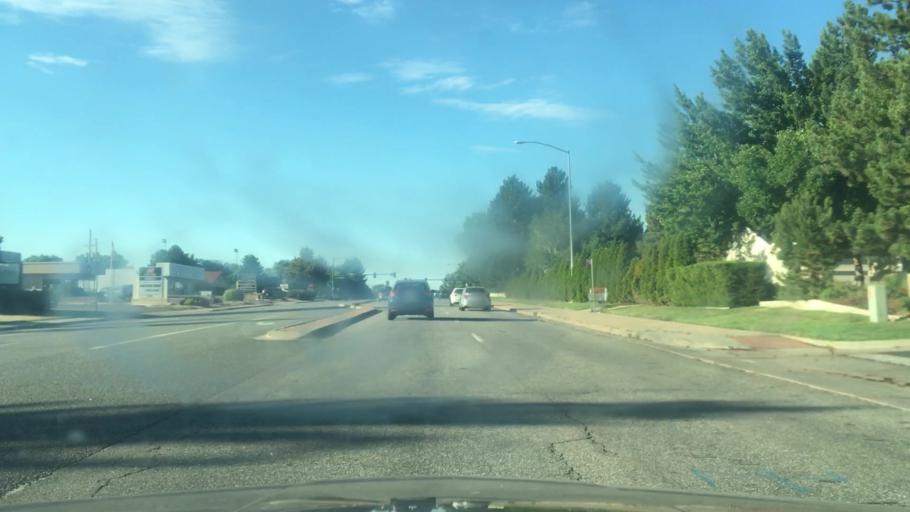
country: US
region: Colorado
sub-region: Arapahoe County
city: Castlewood
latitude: 39.6335
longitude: -104.8853
